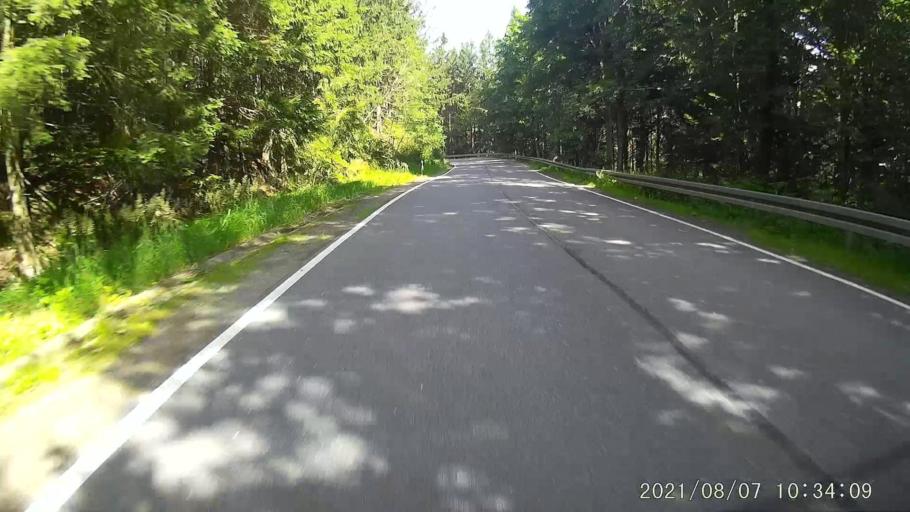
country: PL
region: Lower Silesian Voivodeship
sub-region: Powiat klodzki
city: Duszniki-Zdroj
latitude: 50.3763
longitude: 16.3646
